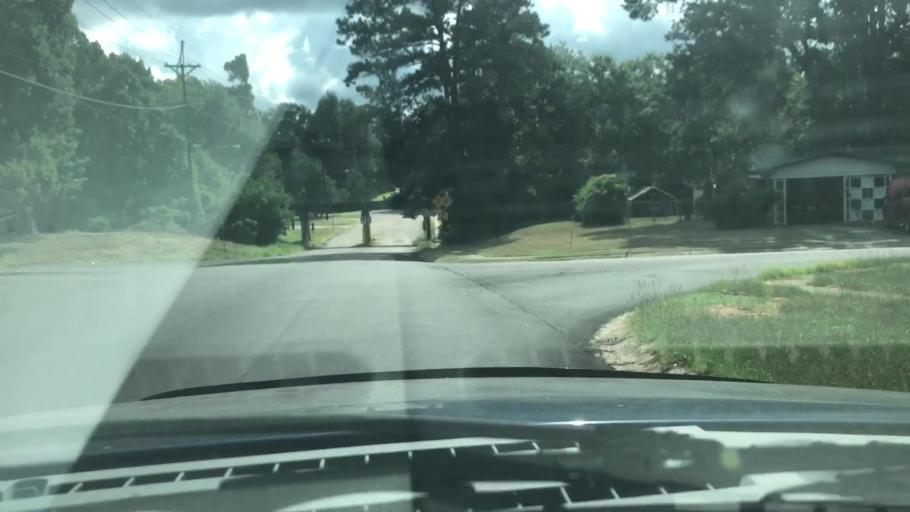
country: US
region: Arkansas
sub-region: Miller County
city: Texarkana
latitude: 33.4556
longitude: -94.0562
